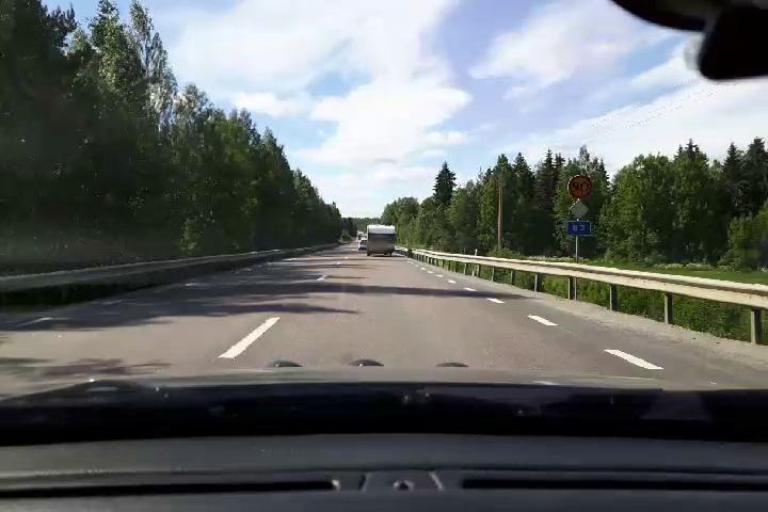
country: SE
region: Gaevleborg
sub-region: Bollnas Kommun
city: Kilafors
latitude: 61.2911
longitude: 16.5029
